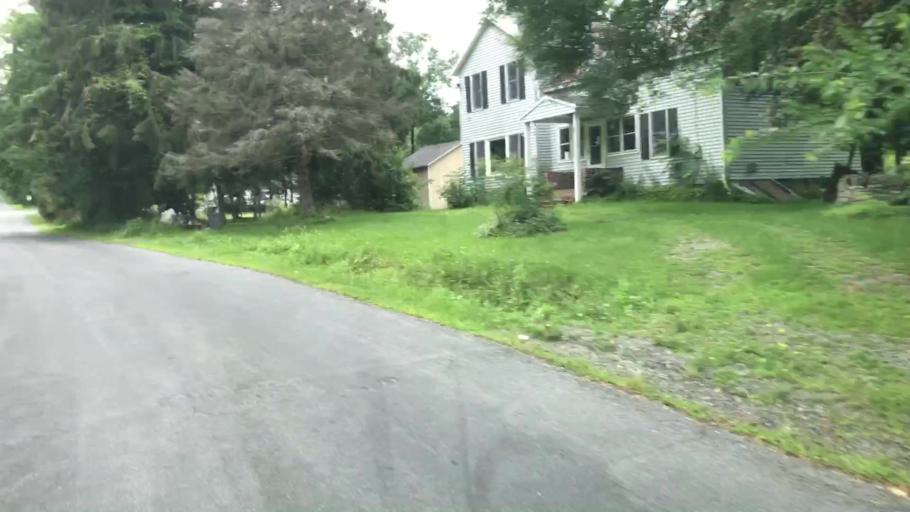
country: US
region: New York
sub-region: Onondaga County
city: Camillus
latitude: 43.0747
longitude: -76.3379
